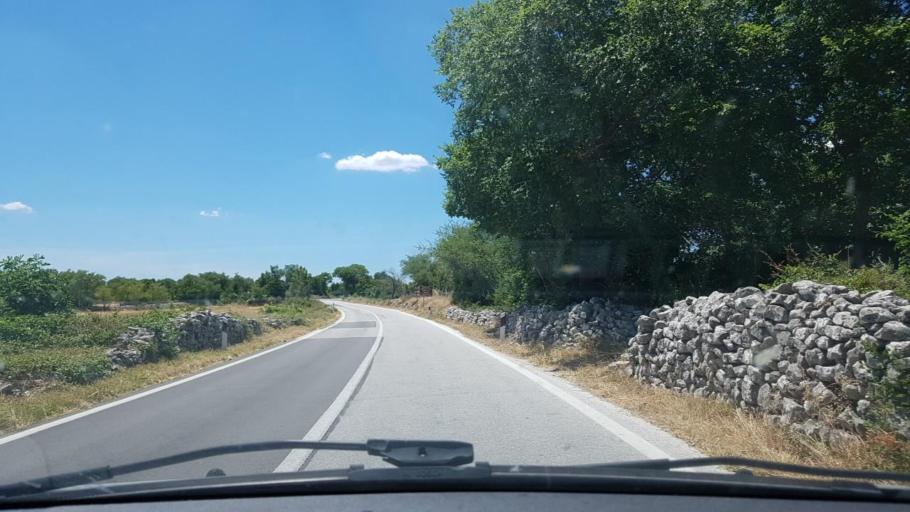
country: HR
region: Sibensko-Kniniska
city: Kistanje
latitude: 44.0186
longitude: 16.0234
